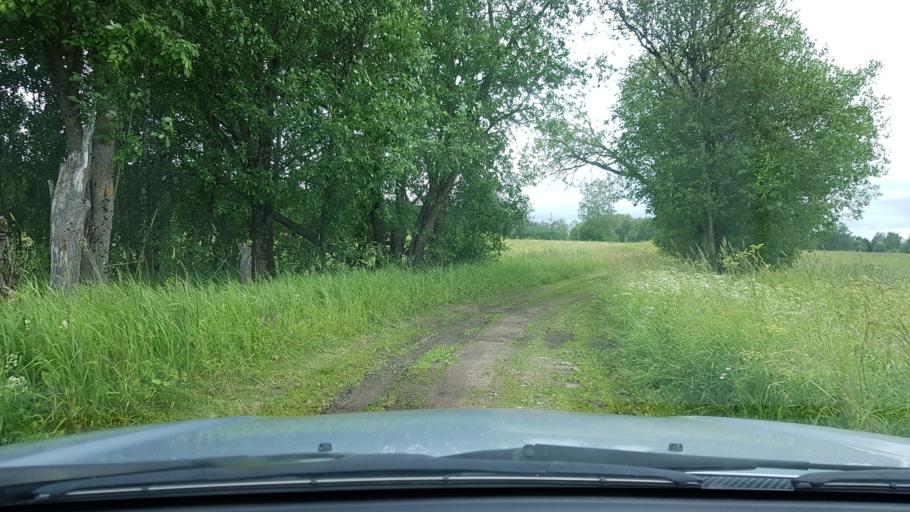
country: EE
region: Ida-Virumaa
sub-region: Narva-Joesuu linn
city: Narva-Joesuu
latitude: 59.3478
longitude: 28.0123
